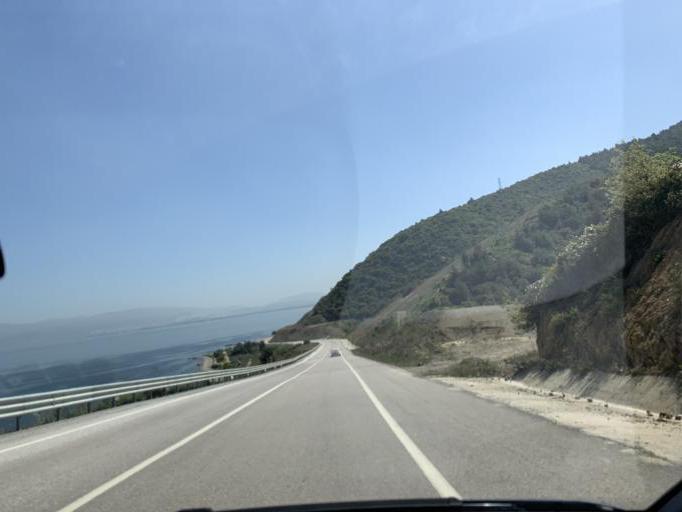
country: TR
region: Bursa
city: Niluefer
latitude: 40.3561
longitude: 28.9872
